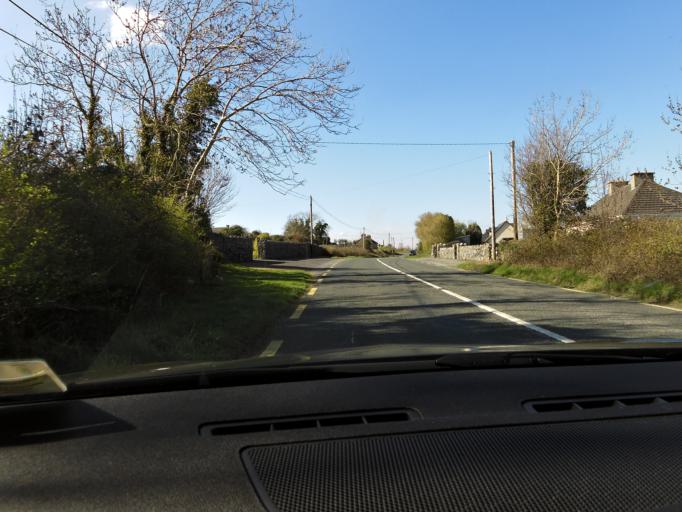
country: IE
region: Connaught
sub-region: County Galway
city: Moycullen
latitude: 53.3656
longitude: -9.2229
